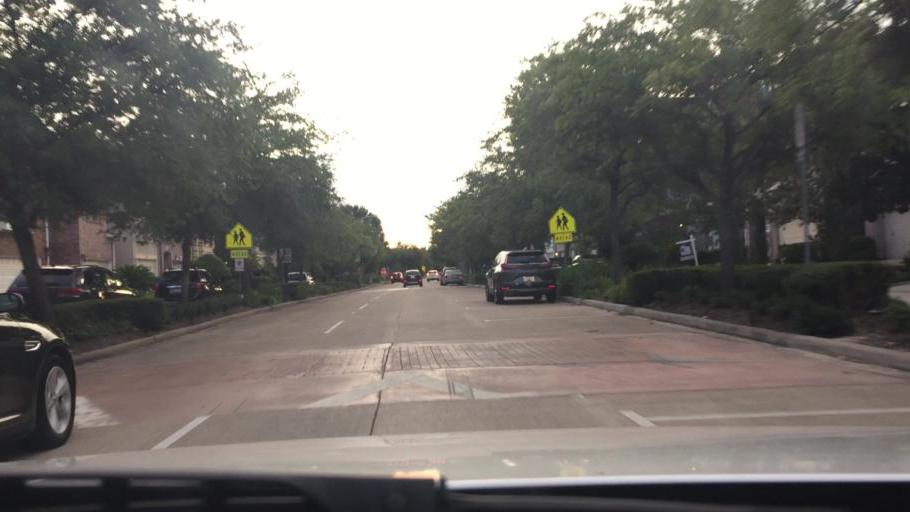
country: US
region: Texas
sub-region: Harris County
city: Bellaire
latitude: 29.7353
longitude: -95.4694
